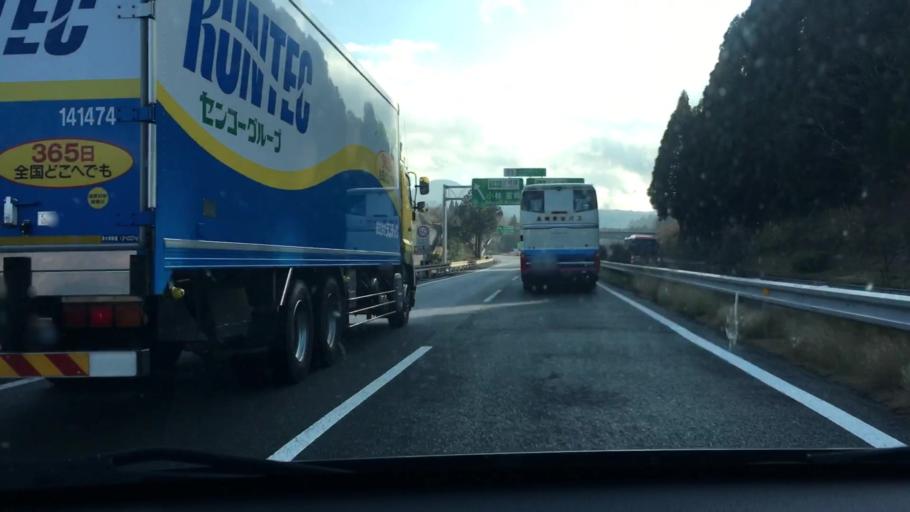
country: JP
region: Kagoshima
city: Okuchi-shinohara
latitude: 32.0379
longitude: 130.7991
